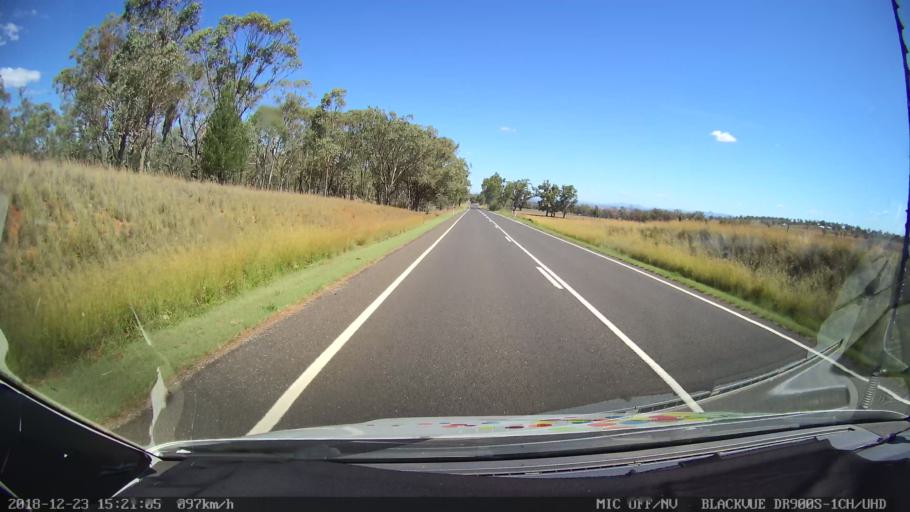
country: AU
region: New South Wales
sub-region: Tamworth Municipality
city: Manilla
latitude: -30.8515
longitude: 150.7941
